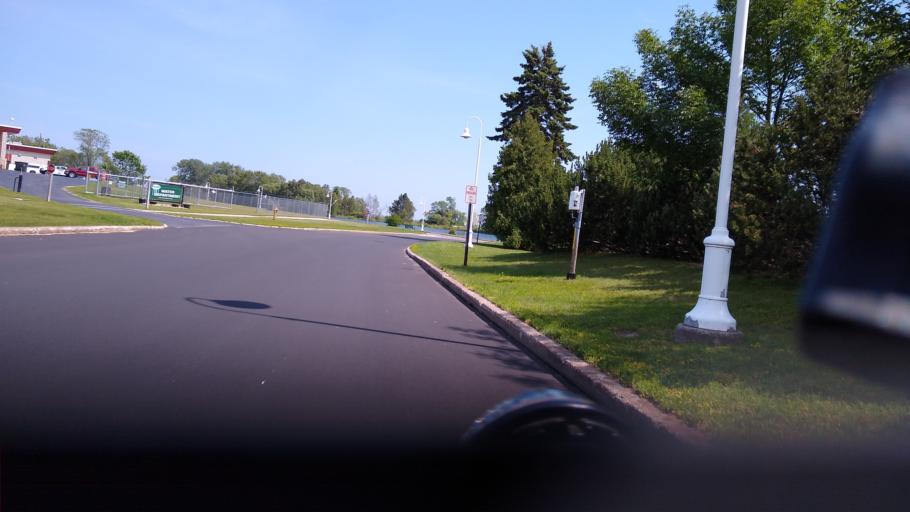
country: US
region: Michigan
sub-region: Delta County
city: Escanaba
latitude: 45.7442
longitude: -87.0426
